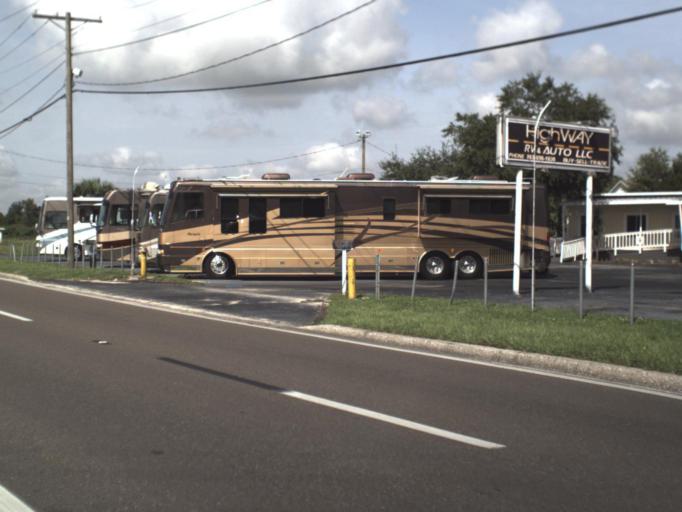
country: US
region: Florida
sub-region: Polk County
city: Lake Alfred
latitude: 28.0762
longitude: -81.7318
